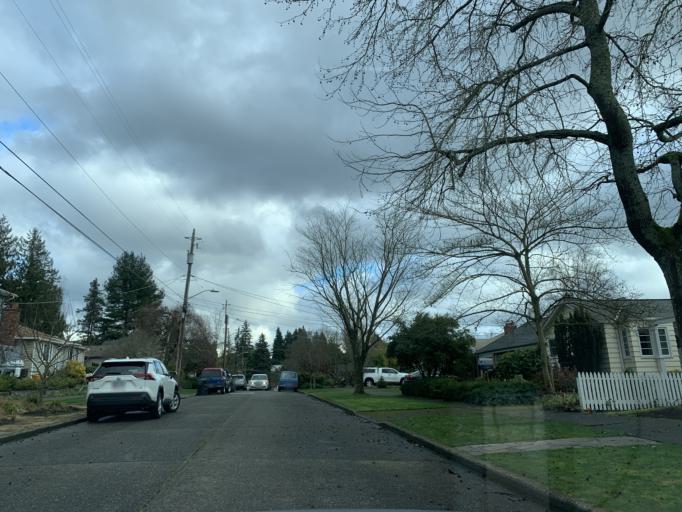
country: US
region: Washington
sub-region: King County
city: Yarrow Point
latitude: 47.6703
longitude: -122.2816
